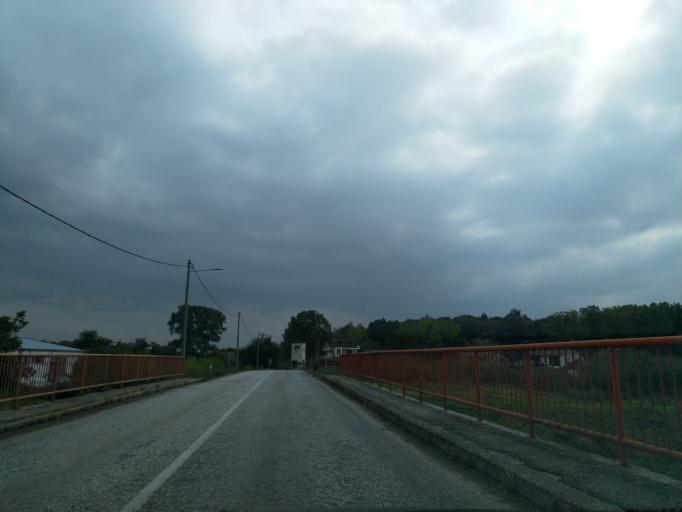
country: RS
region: Central Serbia
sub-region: Sumadijski Okrug
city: Batocina
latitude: 44.1503
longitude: 21.1055
